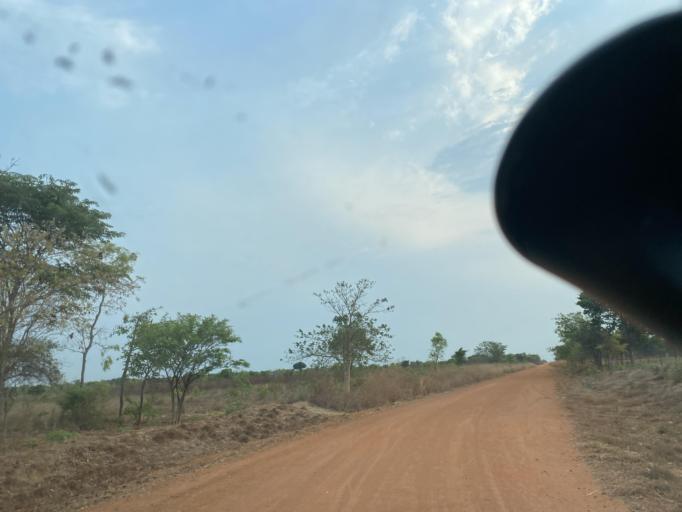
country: ZM
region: Lusaka
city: Chongwe
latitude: -15.2237
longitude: 28.5912
